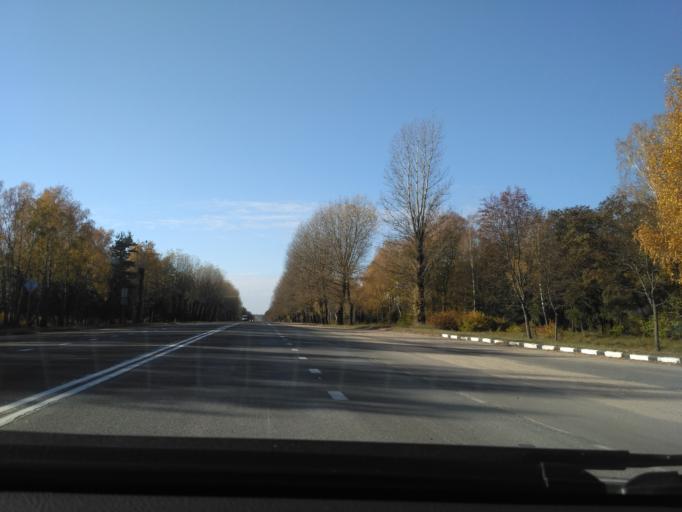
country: BY
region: Minsk
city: Horad Barysaw
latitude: 54.2523
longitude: 28.5618
